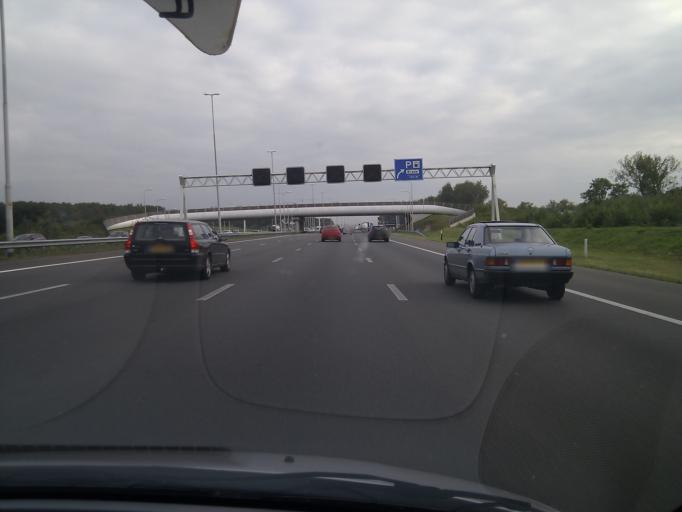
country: NL
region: Gelderland
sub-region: Gemeente Culemborg
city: Culemborg
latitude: 51.9189
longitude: 5.1743
